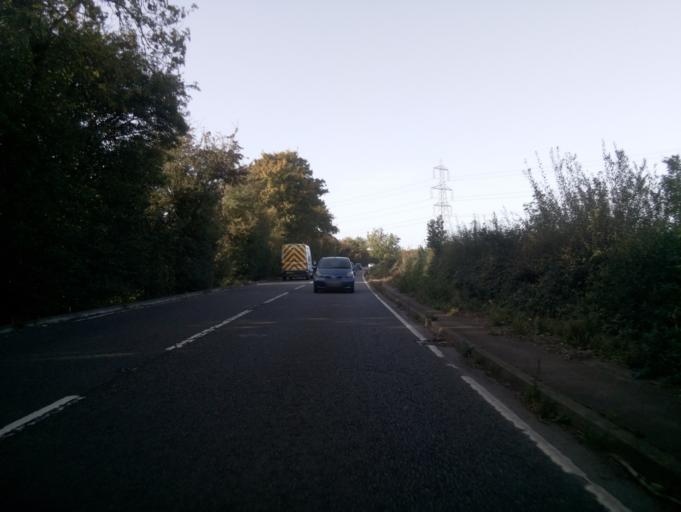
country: GB
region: England
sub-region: Gloucestershire
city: Gloucester
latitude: 51.8800
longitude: -2.2670
